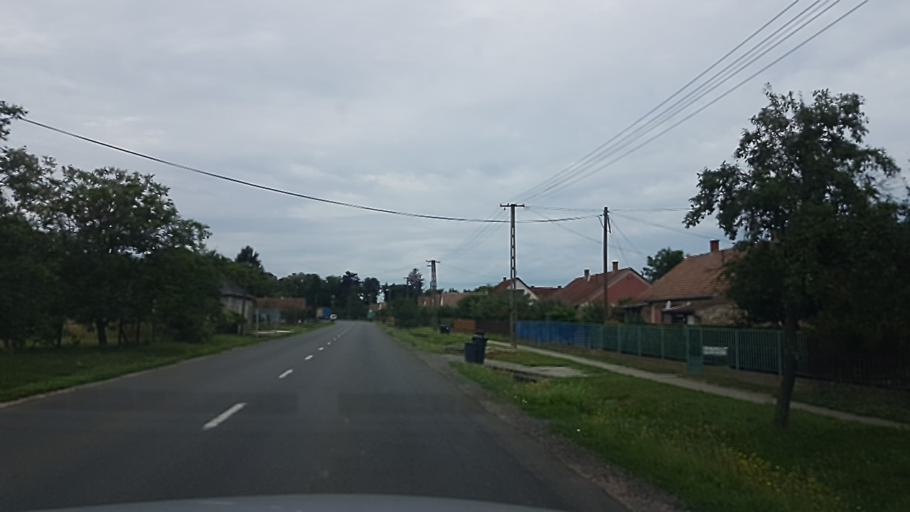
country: HU
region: Baranya
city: Szigetvar
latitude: 46.0348
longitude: 17.7086
